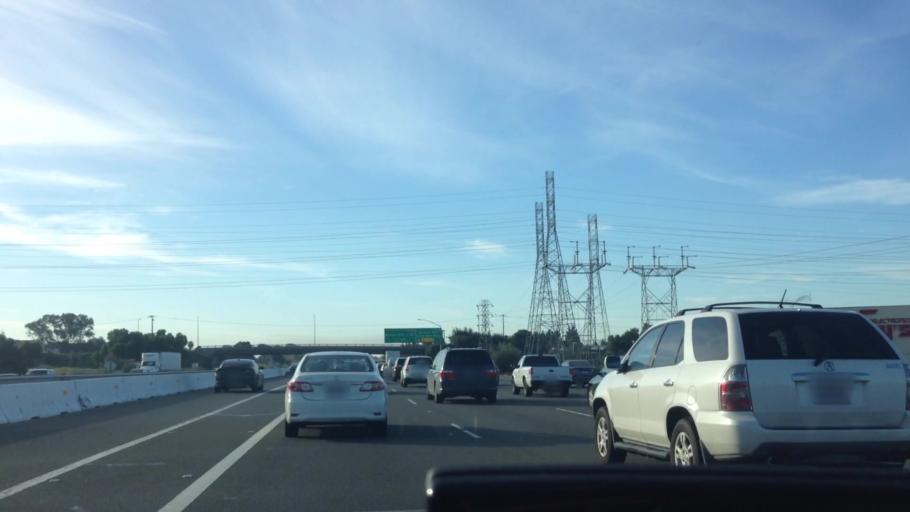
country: US
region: California
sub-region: Alameda County
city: Fremont
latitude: 37.5174
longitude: -121.9414
